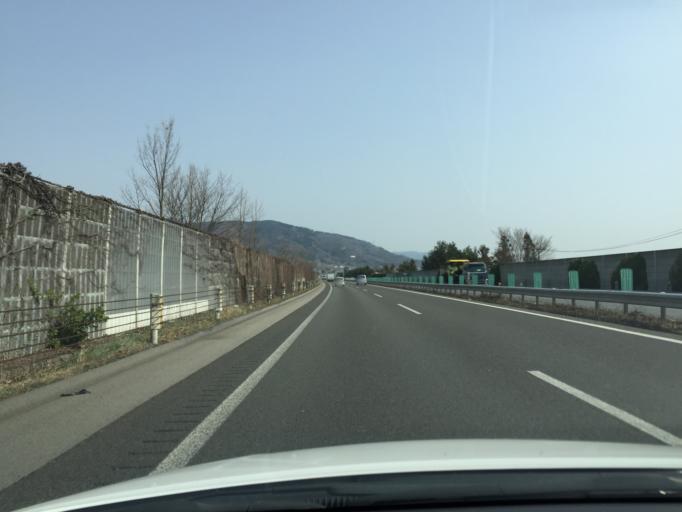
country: JP
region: Fukushima
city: Fukushima-shi
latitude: 37.8108
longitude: 140.4688
